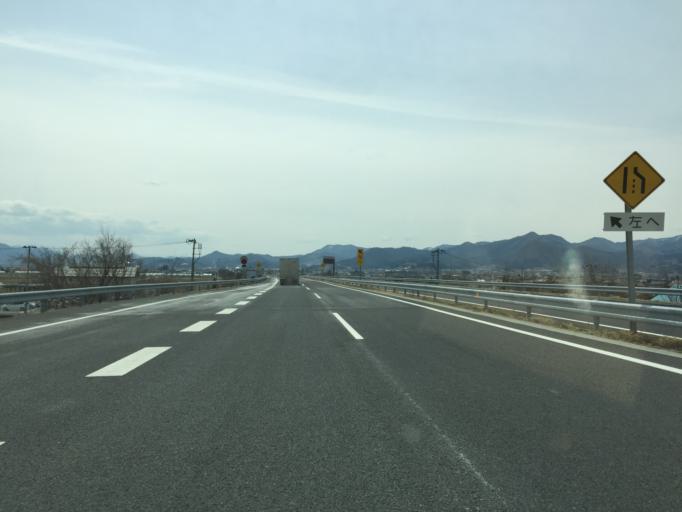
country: JP
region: Yamagata
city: Yamagata-shi
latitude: 38.2686
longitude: 140.2922
